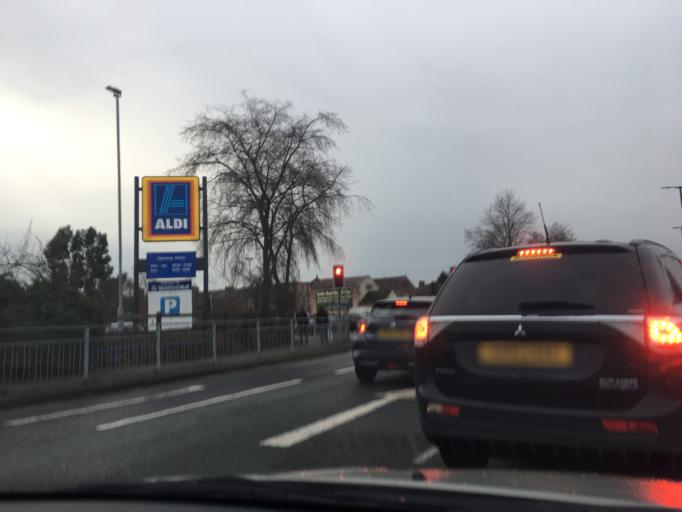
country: GB
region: England
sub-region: Trafford
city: Stretford
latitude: 53.4459
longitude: -2.3121
